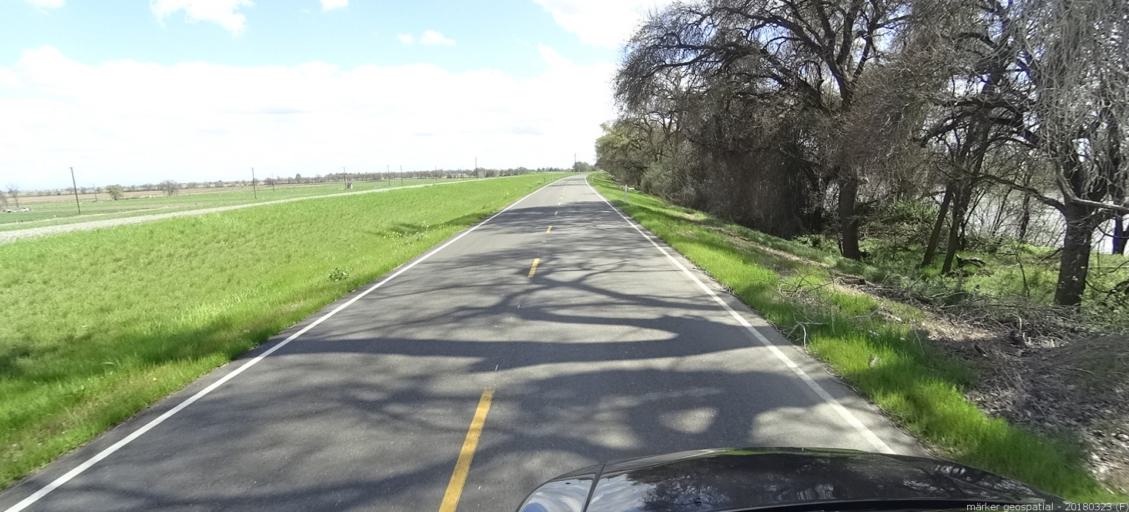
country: US
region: California
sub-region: Yolo County
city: West Sacramento
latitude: 38.6625
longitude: -121.6089
